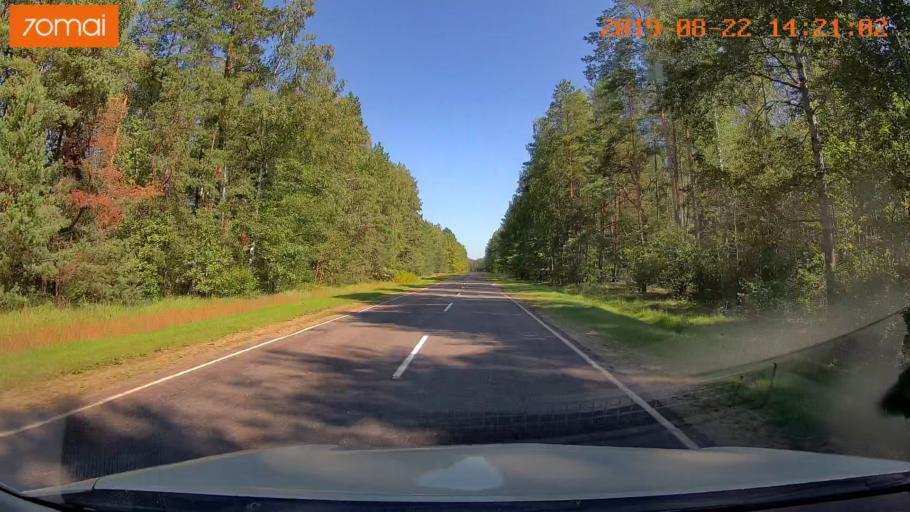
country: BY
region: Mogilev
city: Asipovichy
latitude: 53.2659
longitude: 28.5433
